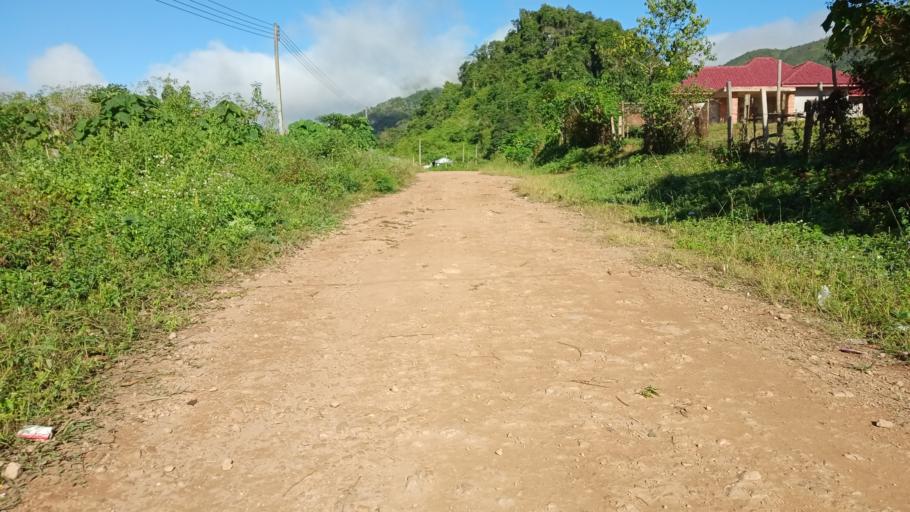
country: LA
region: Xiangkhoang
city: Phonsavan
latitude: 19.1158
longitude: 102.9111
